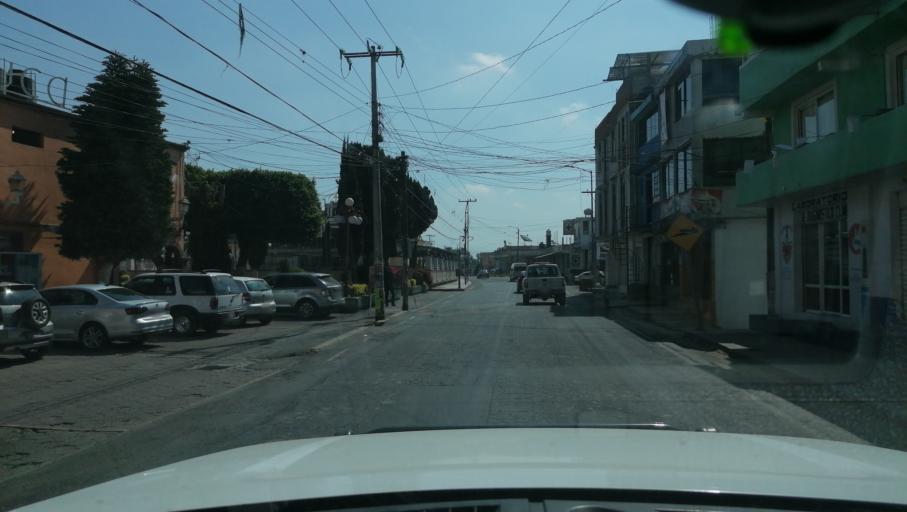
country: MX
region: Tlaxcala
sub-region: Tetlatlahuca
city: Tetlatlahuca
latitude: 19.2315
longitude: -98.2959
